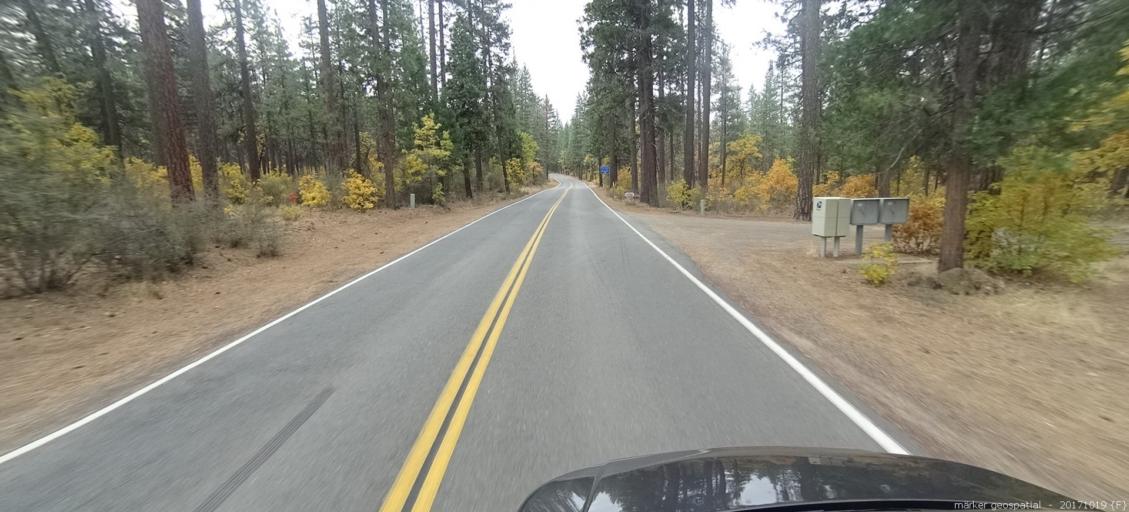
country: US
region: California
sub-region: Shasta County
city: Burney
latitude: 41.1834
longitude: -121.3629
